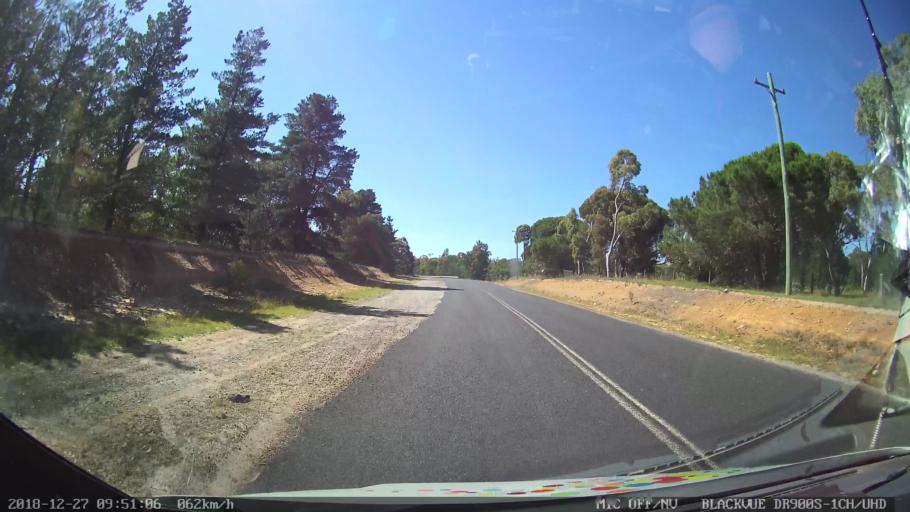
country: AU
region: New South Wales
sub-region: Lithgow
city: Portland
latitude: -33.3660
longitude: 149.9848
